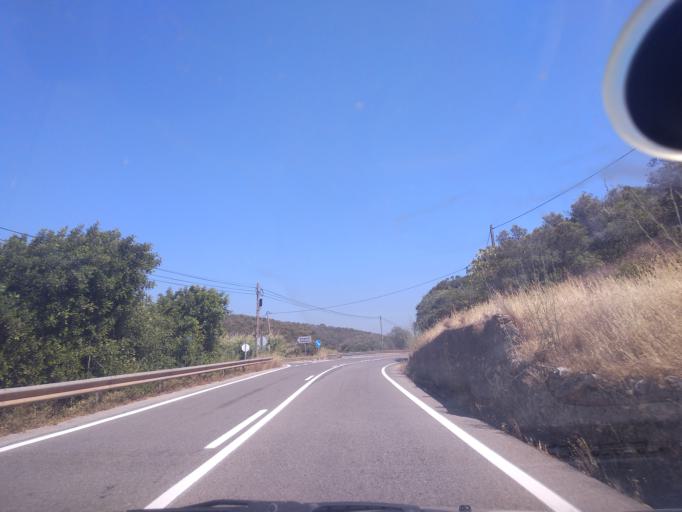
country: PT
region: Faro
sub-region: Lagos
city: Lagos
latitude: 37.1361
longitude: -8.7003
